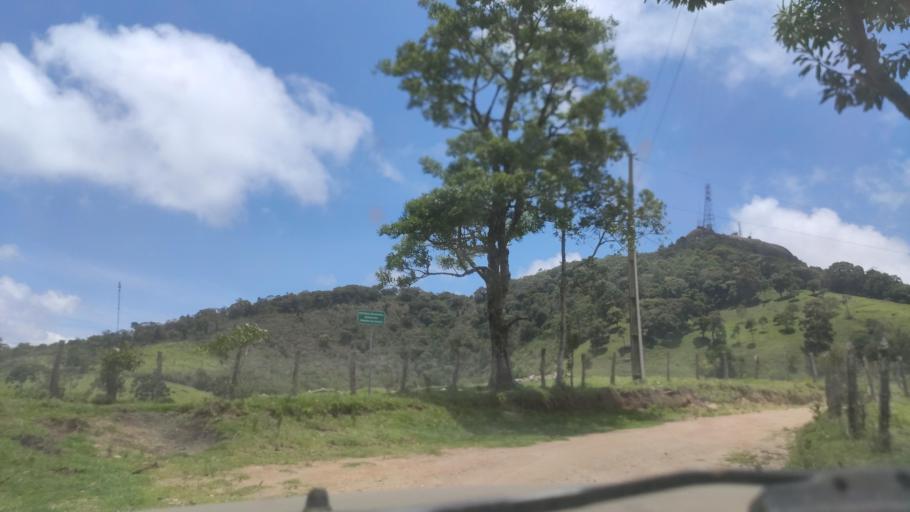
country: BR
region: Minas Gerais
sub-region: Cambui
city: Cambui
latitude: -22.6856
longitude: -45.9560
